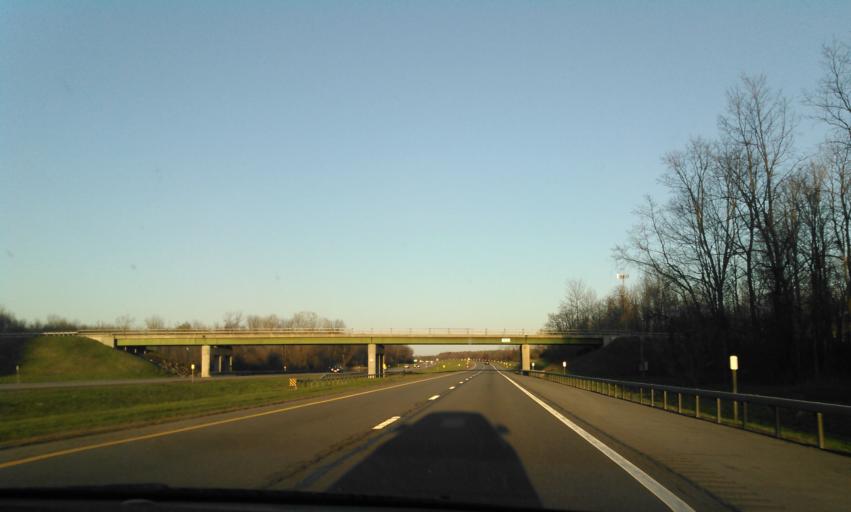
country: US
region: New York
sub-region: Ontario County
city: Manchester
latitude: 42.9813
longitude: -77.2786
